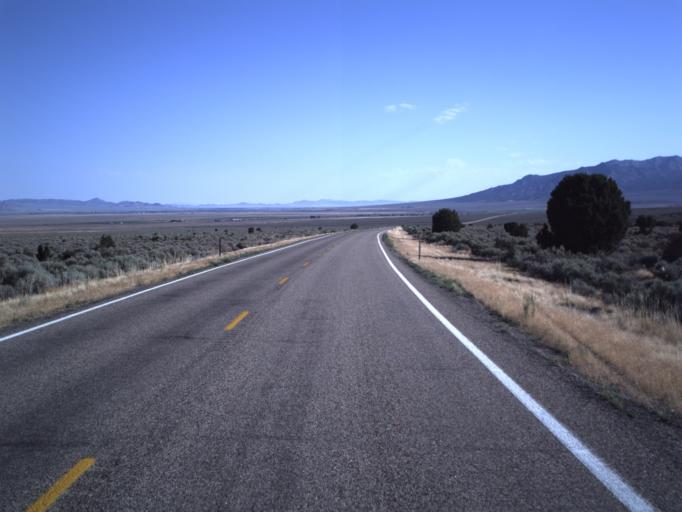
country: US
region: Utah
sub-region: Beaver County
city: Milford
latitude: 38.1350
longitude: -112.9601
